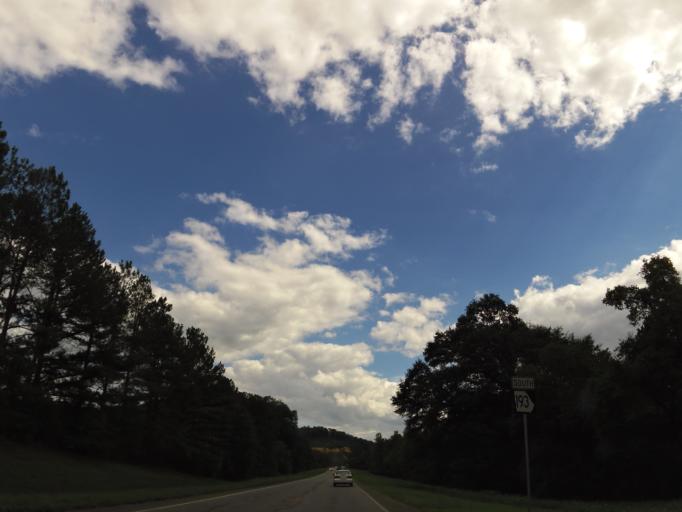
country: US
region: Georgia
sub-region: Walker County
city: Lookout Mountain
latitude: 34.9613
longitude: -85.3370
